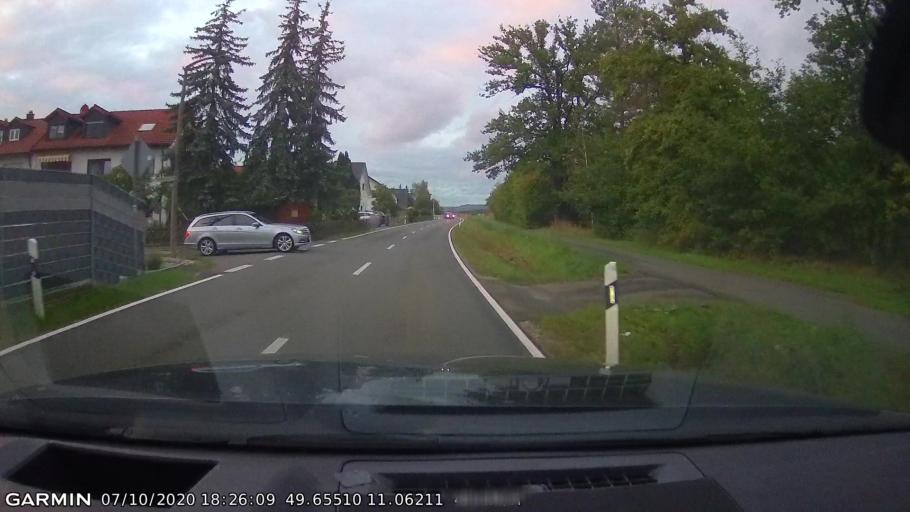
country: DE
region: Bavaria
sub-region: Upper Franconia
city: Poxdorf
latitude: 49.6551
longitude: 11.0621
